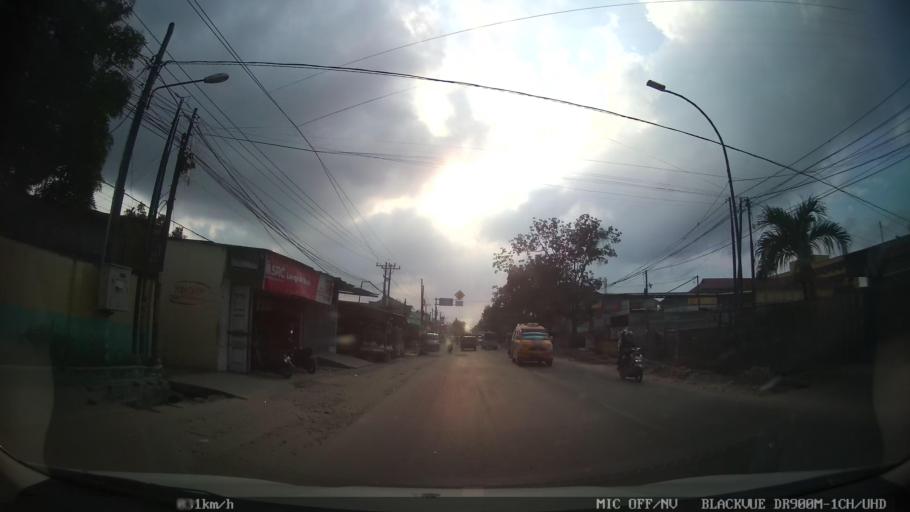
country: ID
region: North Sumatra
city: Medan
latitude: 3.5970
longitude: 98.7377
